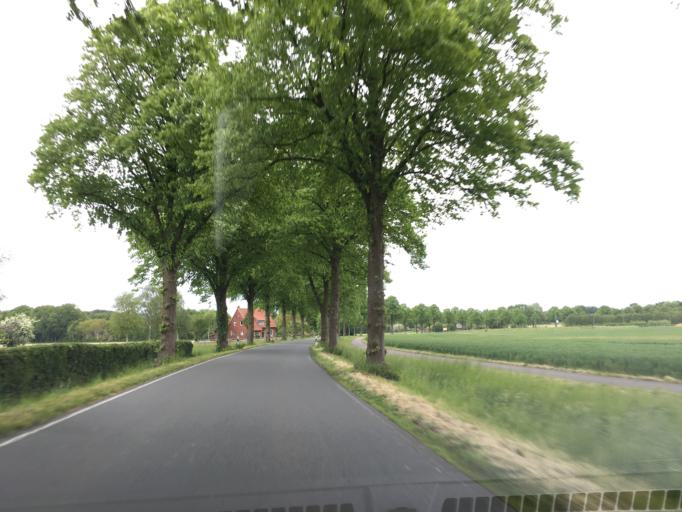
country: DE
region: North Rhine-Westphalia
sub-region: Regierungsbezirk Munster
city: Senden
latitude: 51.9282
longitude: 7.4854
